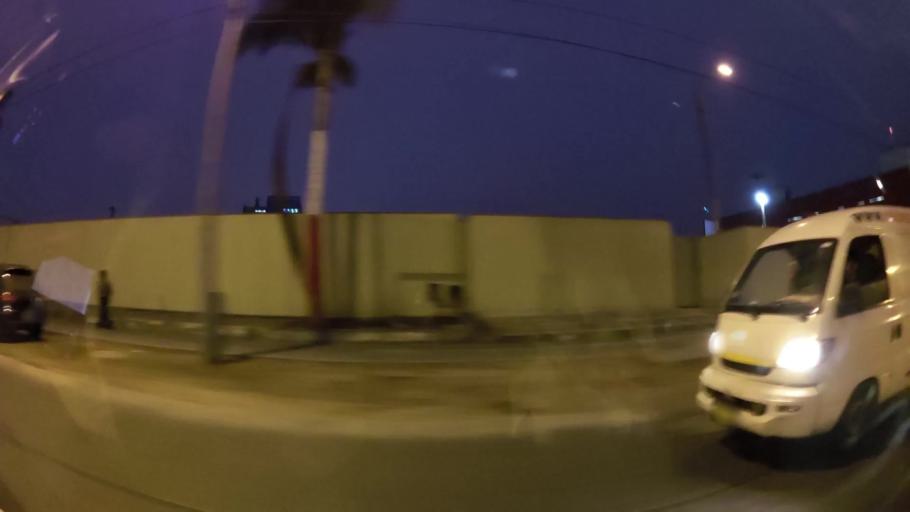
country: PE
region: Callao
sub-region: Callao
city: Callao
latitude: -12.0762
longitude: -77.0927
